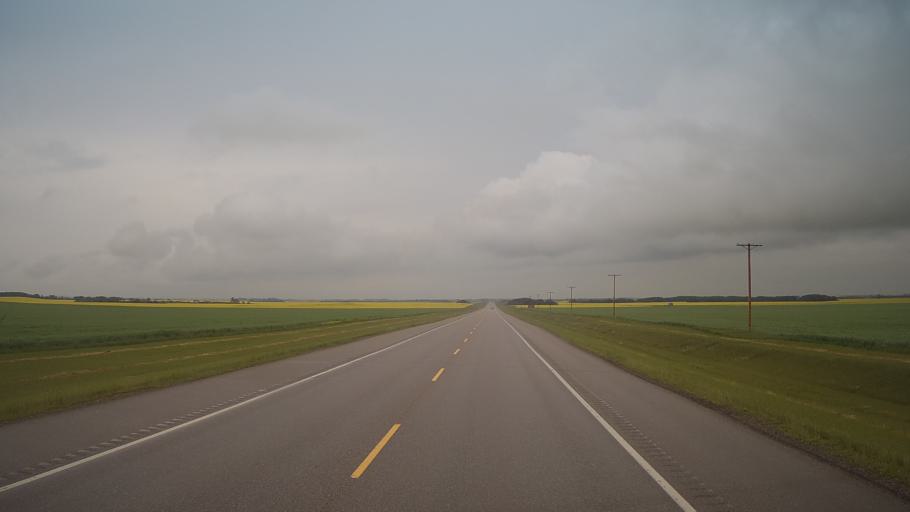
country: CA
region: Saskatchewan
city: Wilkie
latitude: 52.4210
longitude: -108.8964
